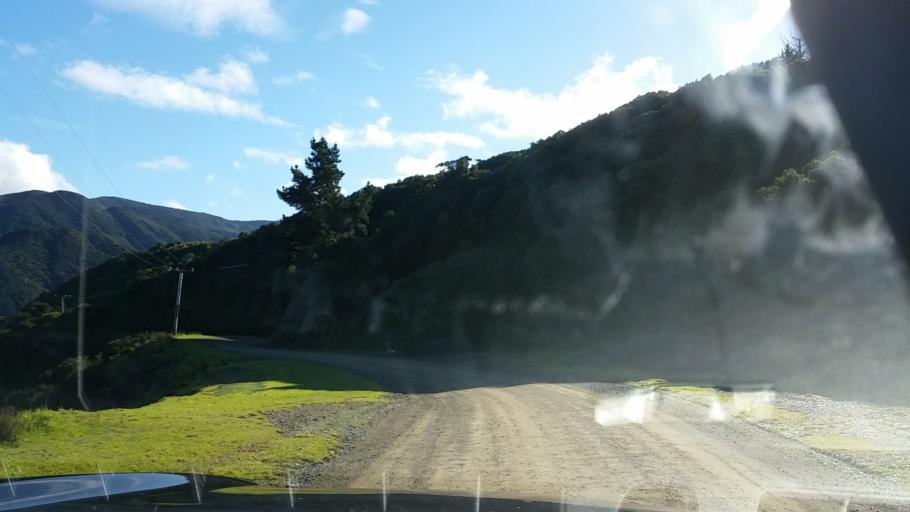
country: NZ
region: Marlborough
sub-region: Marlborough District
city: Picton
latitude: -40.9280
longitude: 173.8385
